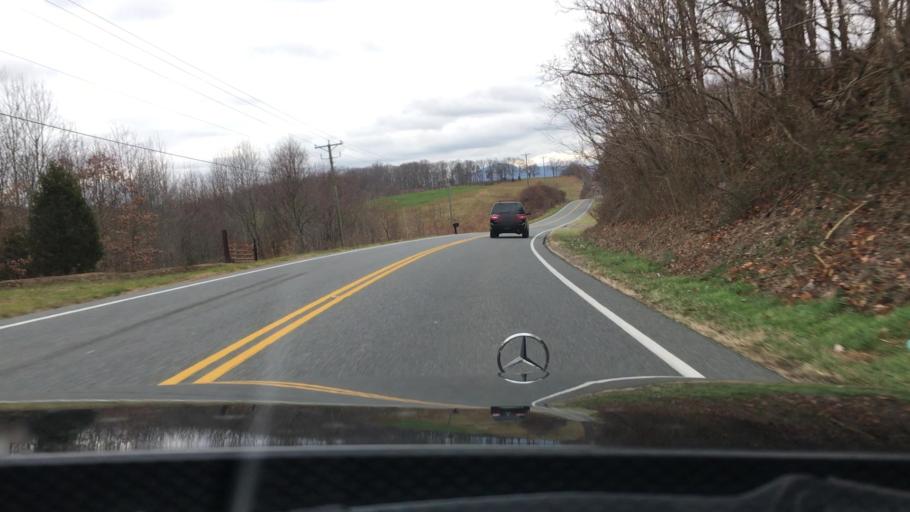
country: US
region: Virginia
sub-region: Franklin County
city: North Shore
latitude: 37.2442
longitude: -79.6807
